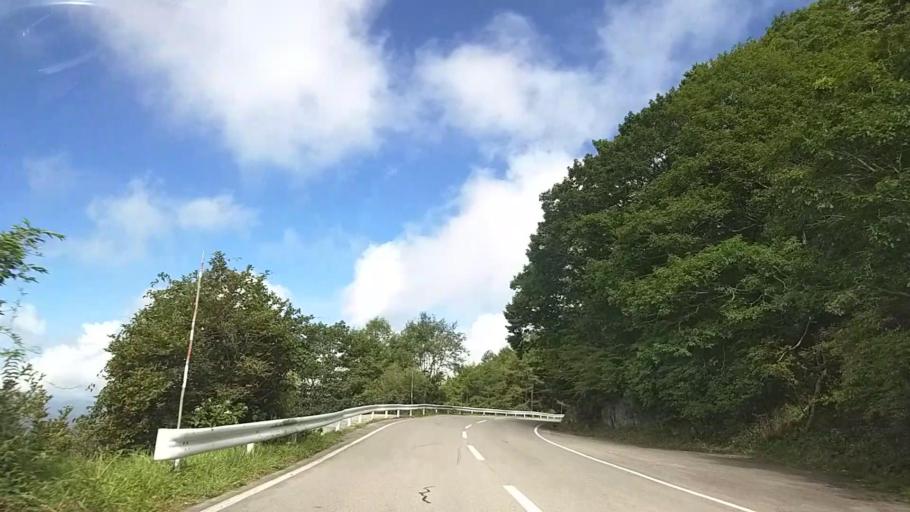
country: JP
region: Nagano
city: Suwa
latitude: 36.1235
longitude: 138.1563
